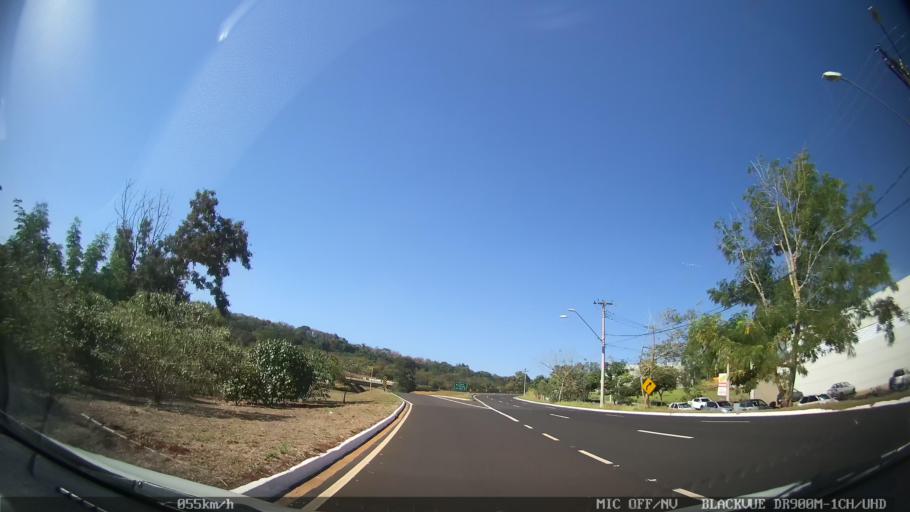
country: BR
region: Sao Paulo
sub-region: Ribeirao Preto
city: Ribeirao Preto
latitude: -21.2381
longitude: -47.7614
